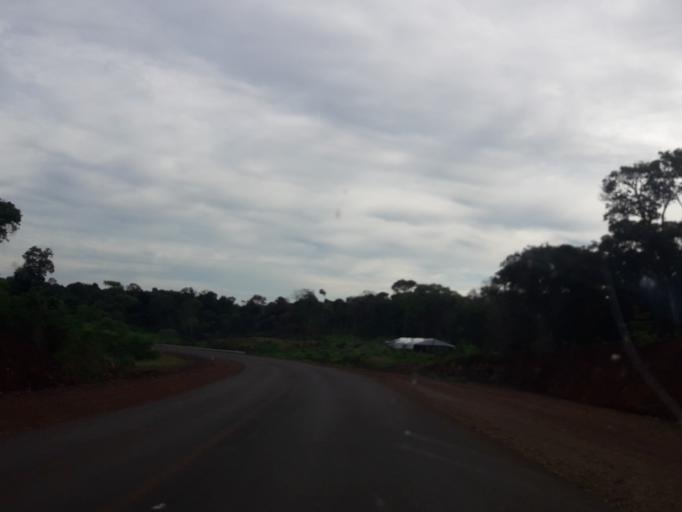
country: AR
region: Misiones
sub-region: Departamento de San Pedro
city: San Pedro
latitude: -26.5092
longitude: -53.9004
